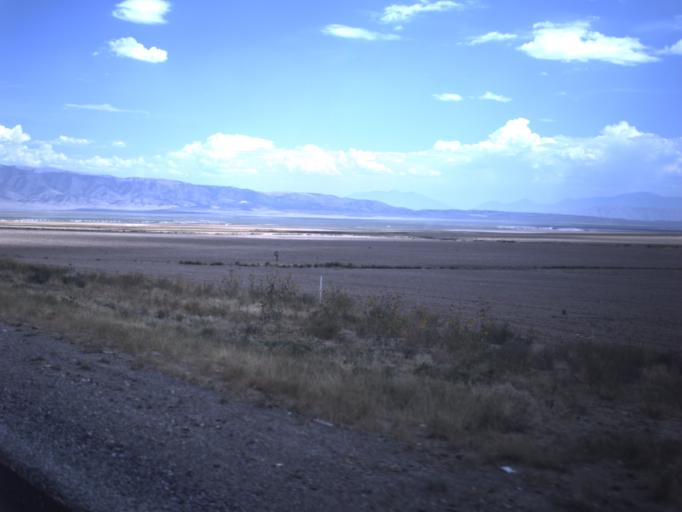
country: US
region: Utah
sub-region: Utah County
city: Eagle Mountain
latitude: 40.2407
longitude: -112.1500
